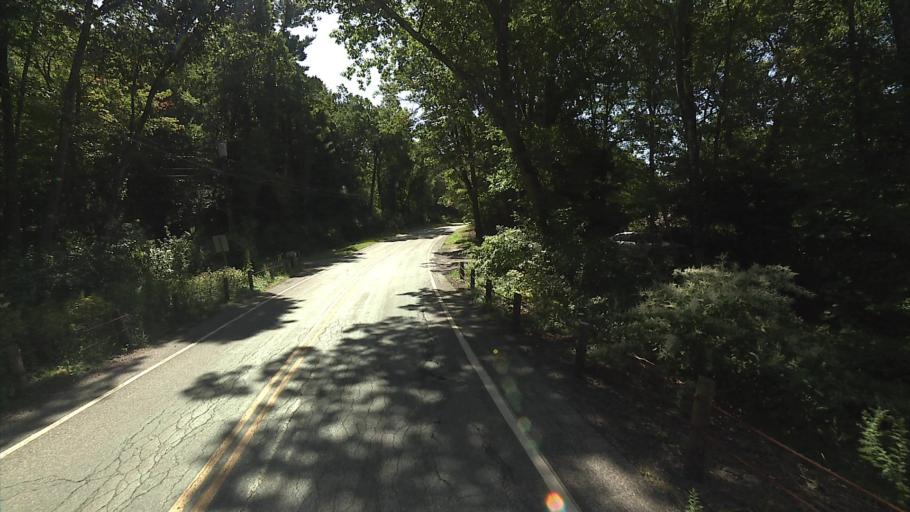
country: US
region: Connecticut
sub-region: Litchfield County
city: Thomaston
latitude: 41.7133
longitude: -73.0681
